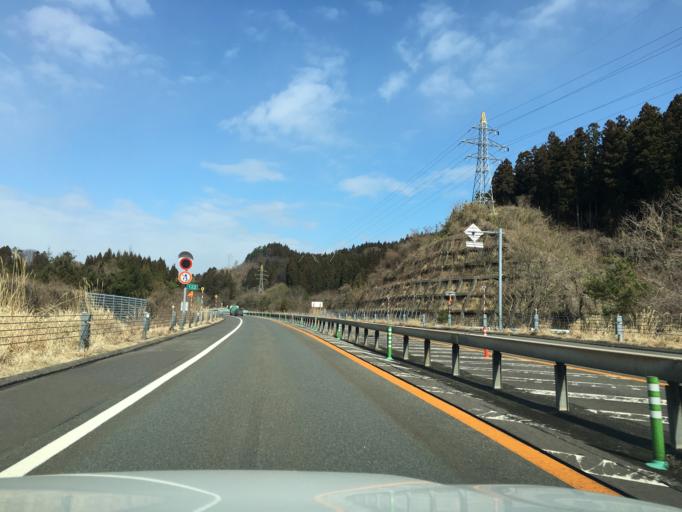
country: JP
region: Akita
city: Akita
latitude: 39.7748
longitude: 140.1196
